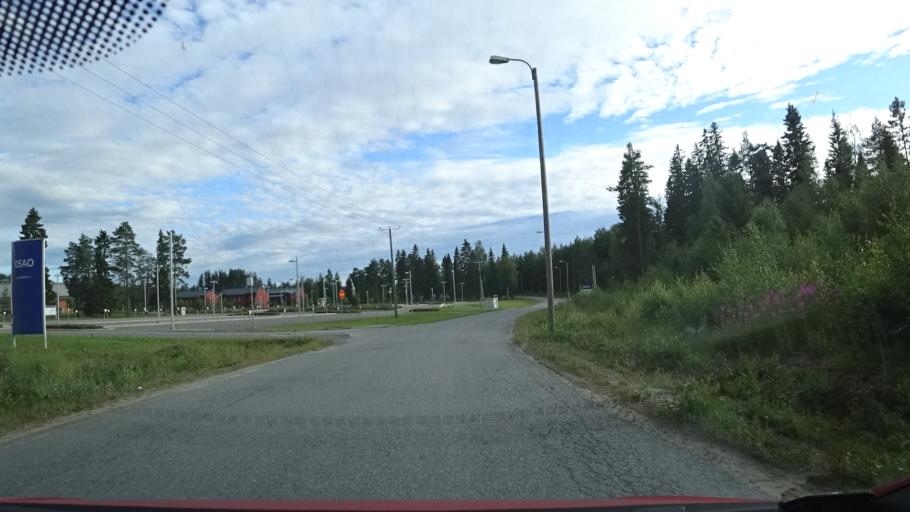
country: FI
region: Northern Ostrobothnia
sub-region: Oulu
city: Haukipudas
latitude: 65.1971
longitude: 25.4132
